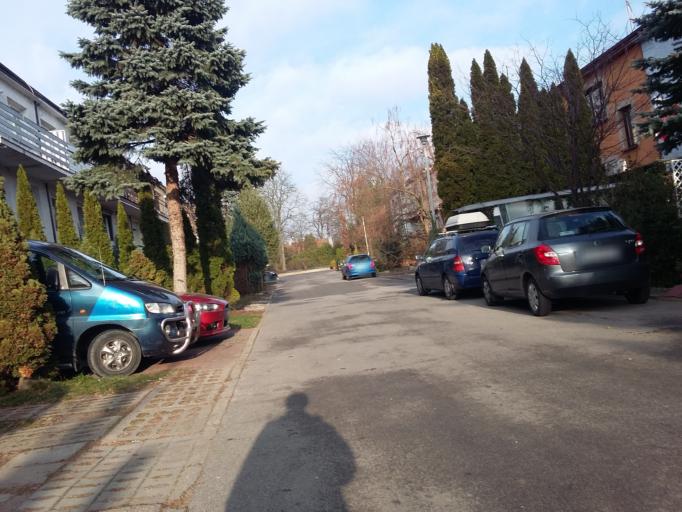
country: PL
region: Lodz Voivodeship
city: Lodz
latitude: 51.7406
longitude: 19.4137
